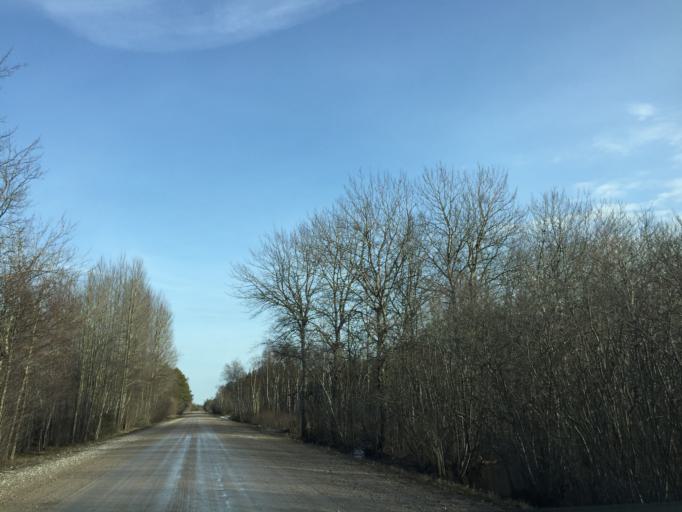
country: EE
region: Saare
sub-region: Kuressaare linn
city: Kuressaare
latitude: 58.3175
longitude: 21.9922
